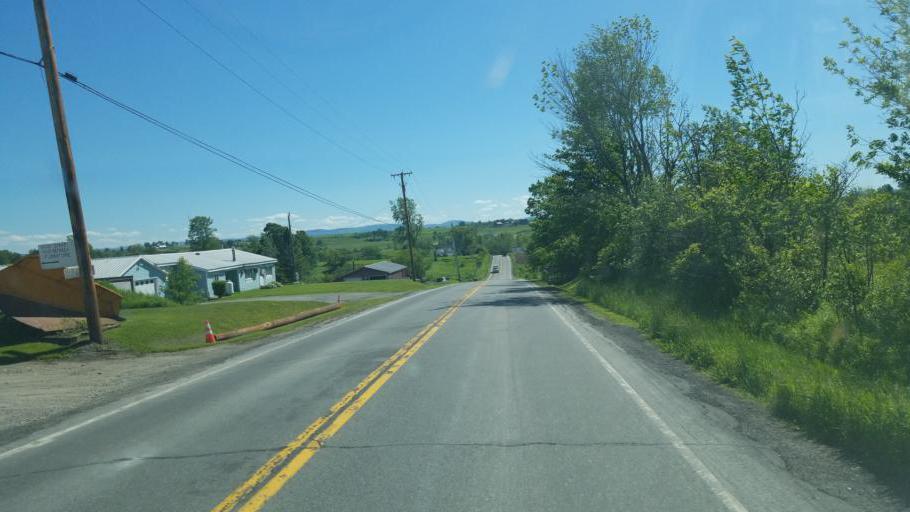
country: US
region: New York
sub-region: Montgomery County
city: Canajoharie
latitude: 42.9781
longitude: -74.5429
